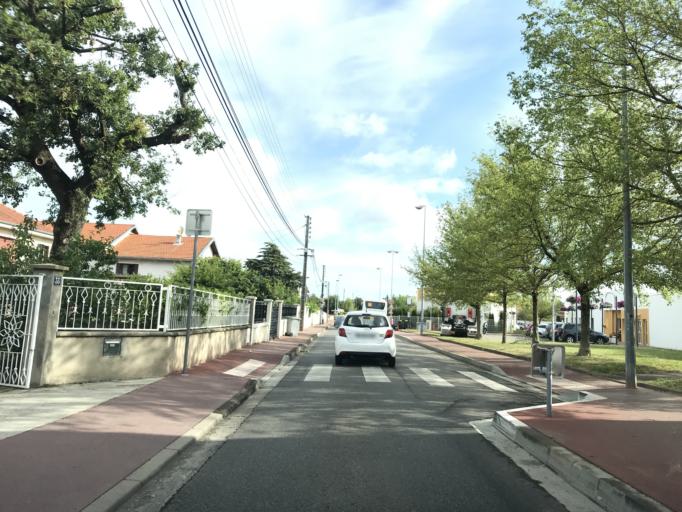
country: FR
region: Rhone-Alpes
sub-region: Departement du Rhone
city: Mions
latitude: 45.6584
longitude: 4.9489
